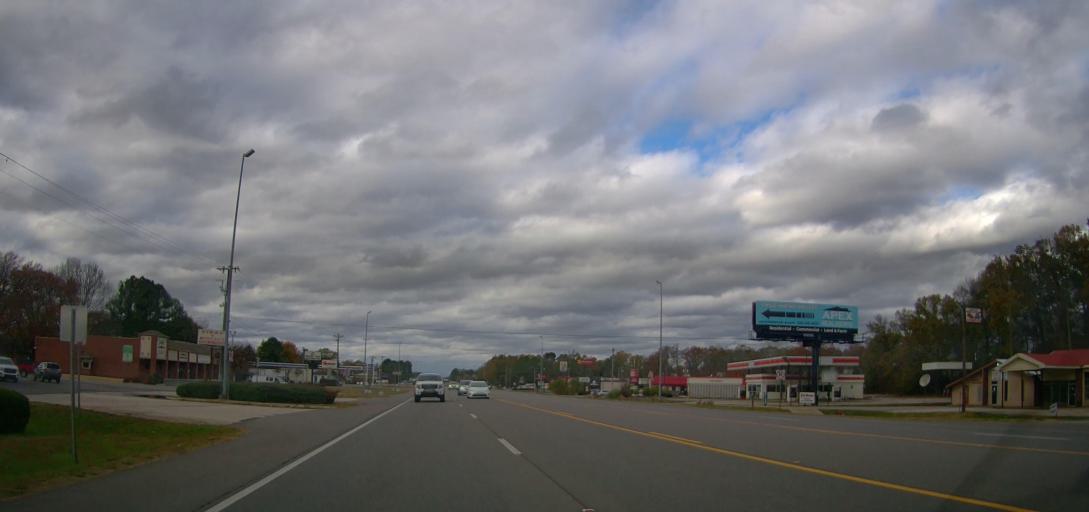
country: US
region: Alabama
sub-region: Lawrence County
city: Moulton
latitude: 34.4856
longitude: -87.2753
